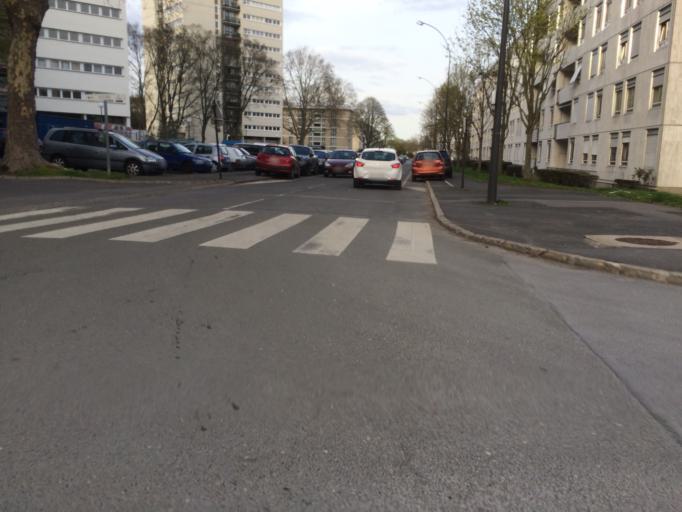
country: FR
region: Ile-de-France
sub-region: Departement de l'Essonne
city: Massy
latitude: 48.7297
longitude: 2.2850
